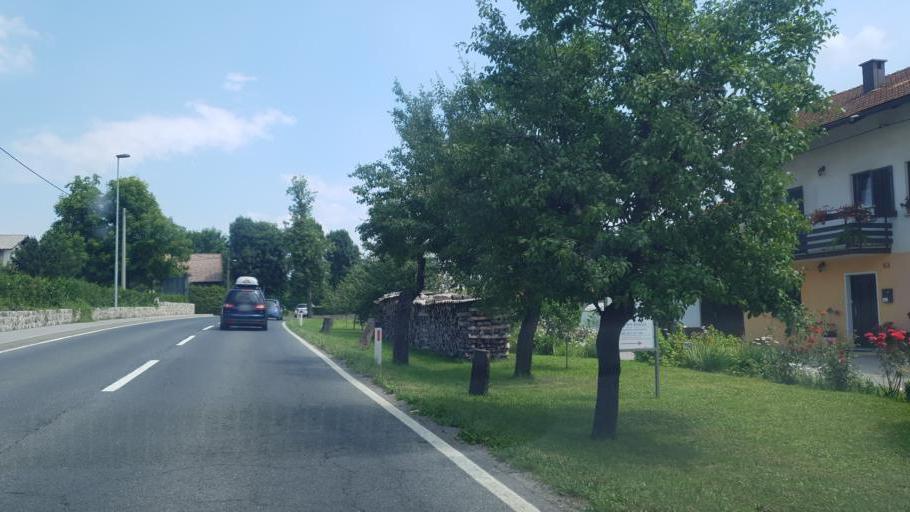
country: SI
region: Postojna
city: Postojna
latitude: 45.7389
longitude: 14.1904
